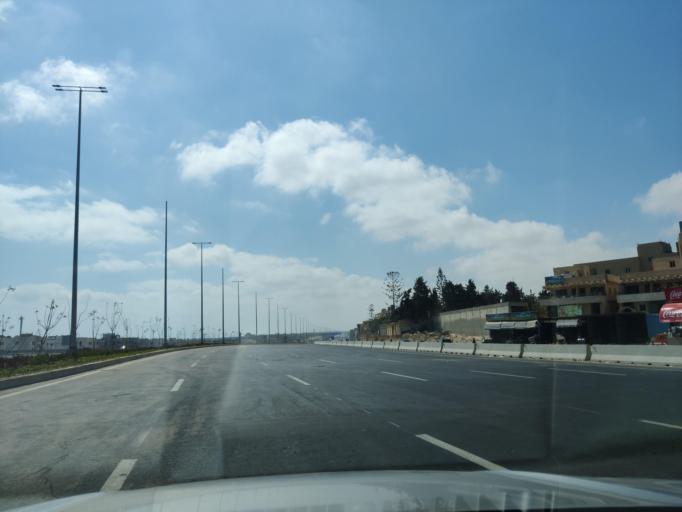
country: EG
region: Muhafazat Matruh
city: Al `Alamayn
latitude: 30.9752
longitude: 28.7305
